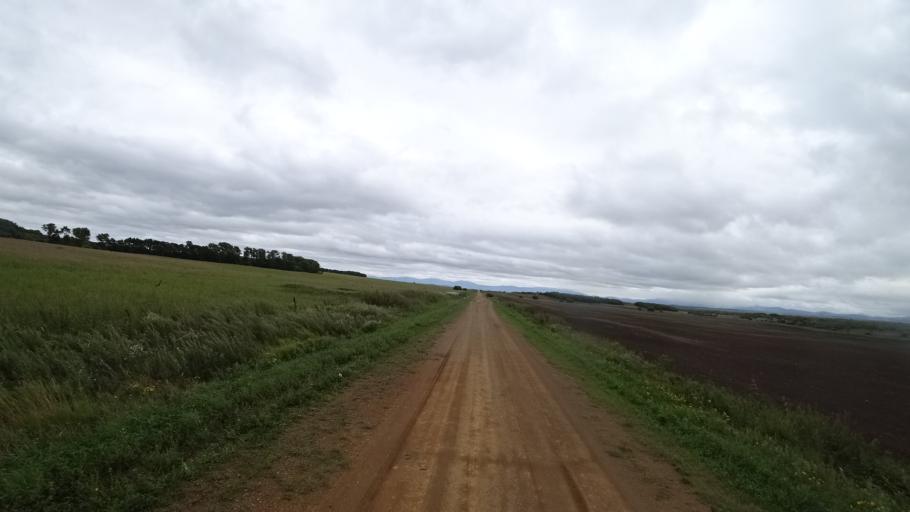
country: RU
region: Primorskiy
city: Chernigovka
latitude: 44.4376
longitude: 132.5788
